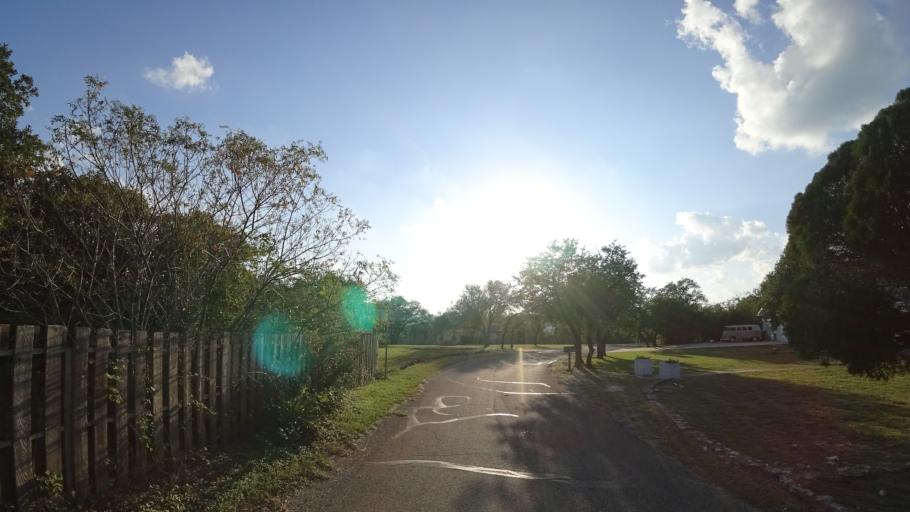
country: US
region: Texas
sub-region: Travis County
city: Lost Creek
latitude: 30.2957
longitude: -97.8460
